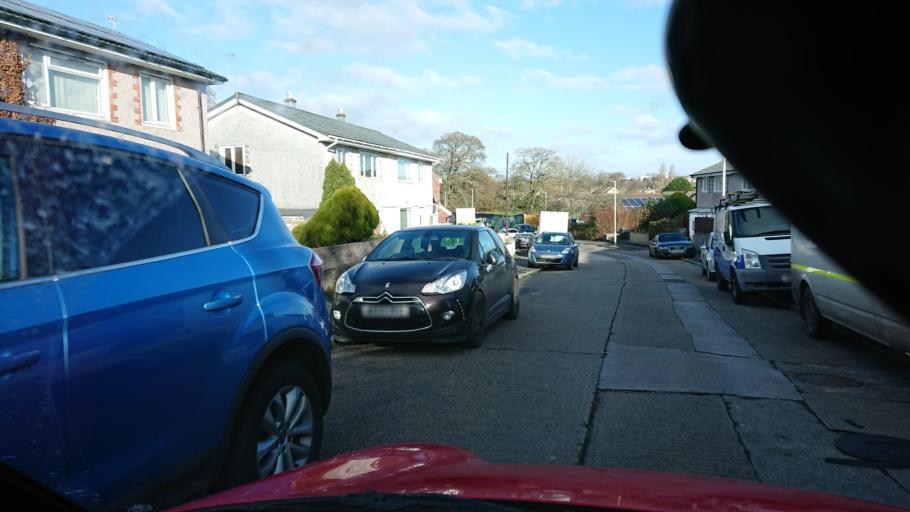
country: GB
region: England
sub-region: Plymouth
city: Plymouth
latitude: 50.4095
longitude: -4.1596
